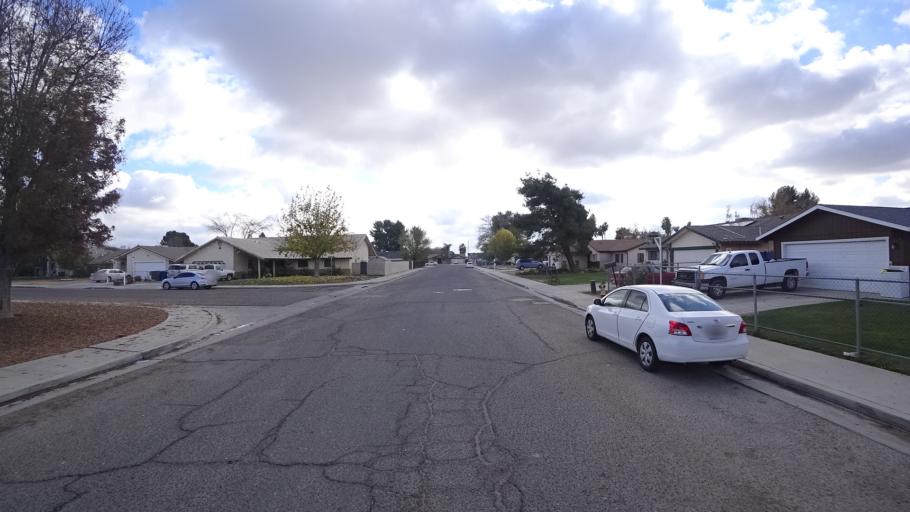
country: US
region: California
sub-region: Kern County
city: Bakersfield
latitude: 35.3567
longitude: -118.9439
